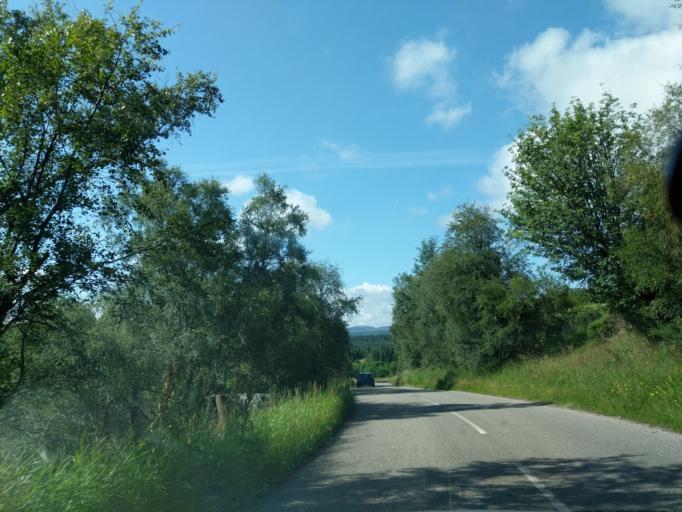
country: GB
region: Scotland
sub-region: Moray
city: Dufftown
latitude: 57.3691
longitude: -3.2577
